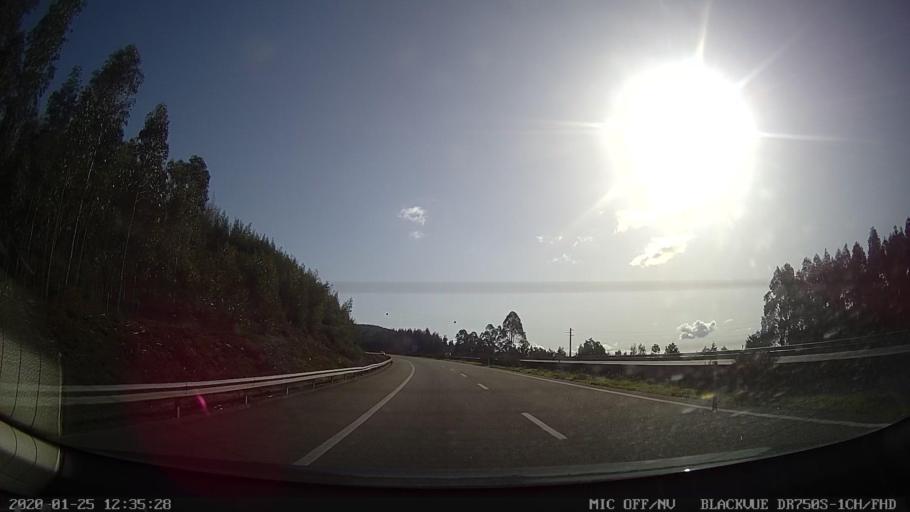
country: PT
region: Aveiro
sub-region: Agueda
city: Valongo
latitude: 40.6632
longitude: -8.3923
